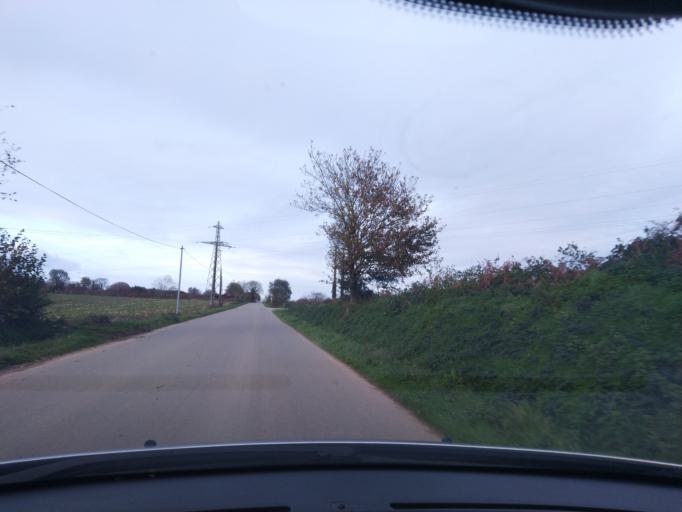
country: FR
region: Brittany
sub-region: Departement du Finistere
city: Guerlesquin
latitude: 48.5498
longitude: -3.6197
